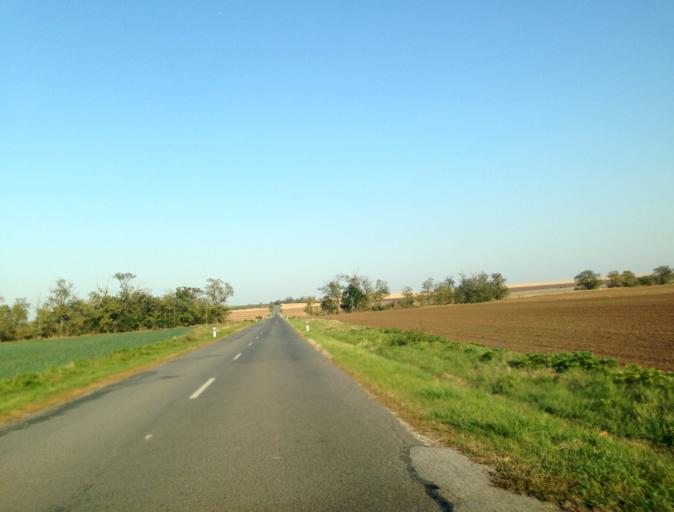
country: SK
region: Nitriansky
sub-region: Okres Komarno
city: Hurbanovo
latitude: 47.8956
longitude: 18.2580
